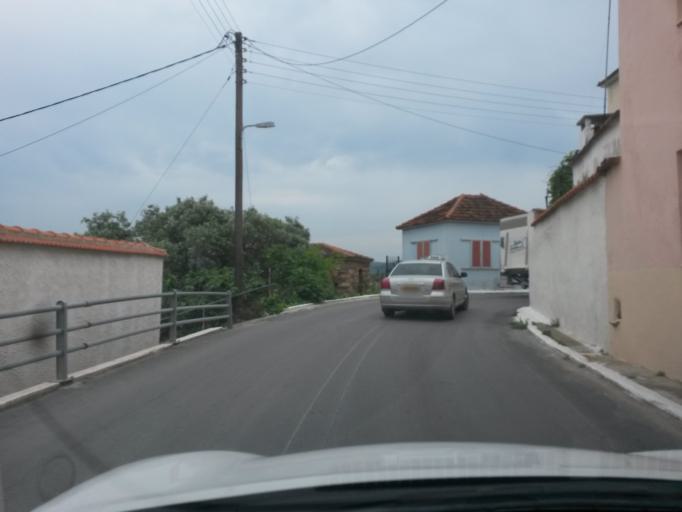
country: GR
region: North Aegean
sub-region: Nomos Lesvou
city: Palaiokipos
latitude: 39.0558
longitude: 26.4529
